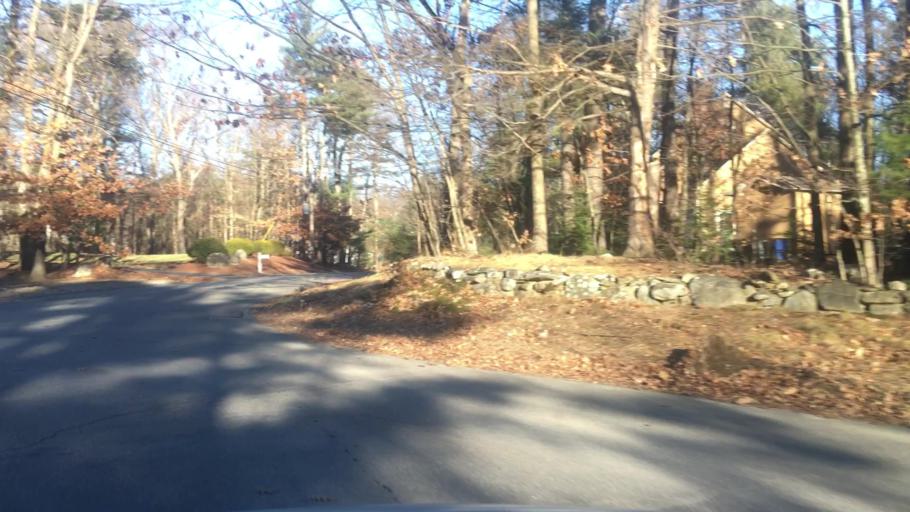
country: US
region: New Hampshire
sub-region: Rockingham County
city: Londonderry
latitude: 42.8810
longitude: -71.3747
